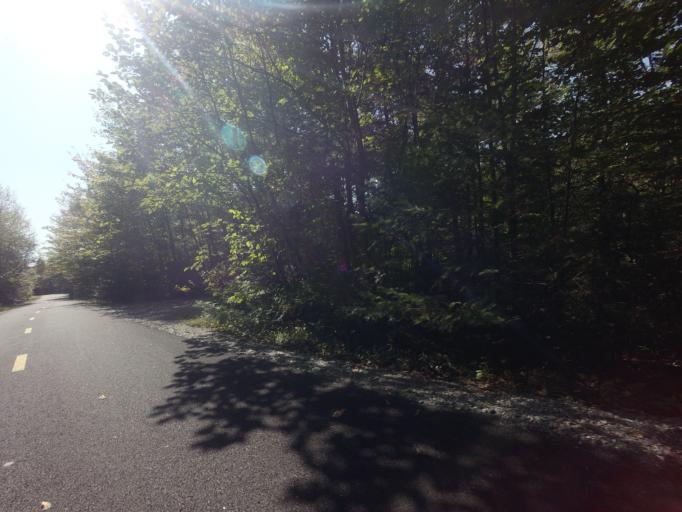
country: CA
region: Quebec
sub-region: Laurentides
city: Mont-Tremblant
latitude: 46.1202
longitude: -74.5015
